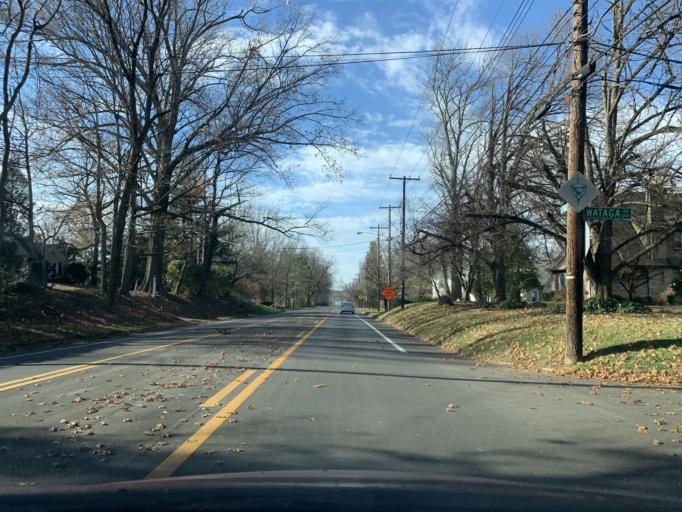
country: US
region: Kentucky
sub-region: Jefferson County
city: Saint Matthews
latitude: 38.2452
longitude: -85.6910
